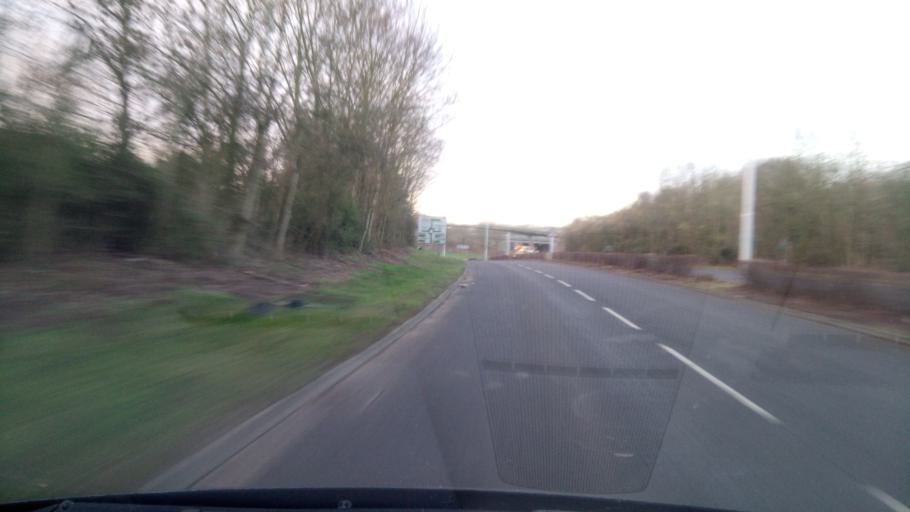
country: GB
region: England
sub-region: Peterborough
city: Marholm
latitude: 52.5740
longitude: -0.2959
